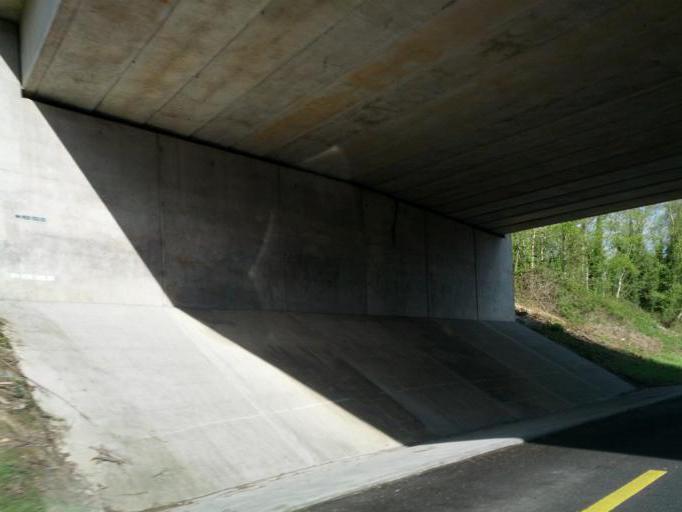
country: IE
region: Leinster
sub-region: An Iarmhi
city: Athlone
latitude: 53.4315
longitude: -7.9248
